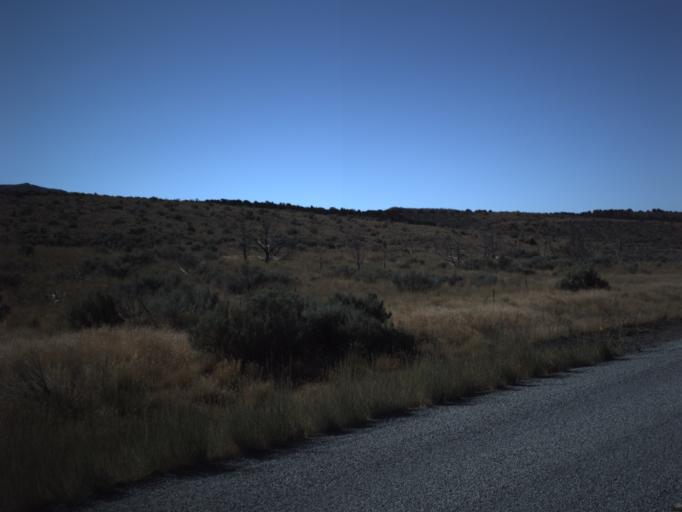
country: US
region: Utah
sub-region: Juab County
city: Mona
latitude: 39.7903
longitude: -112.1489
